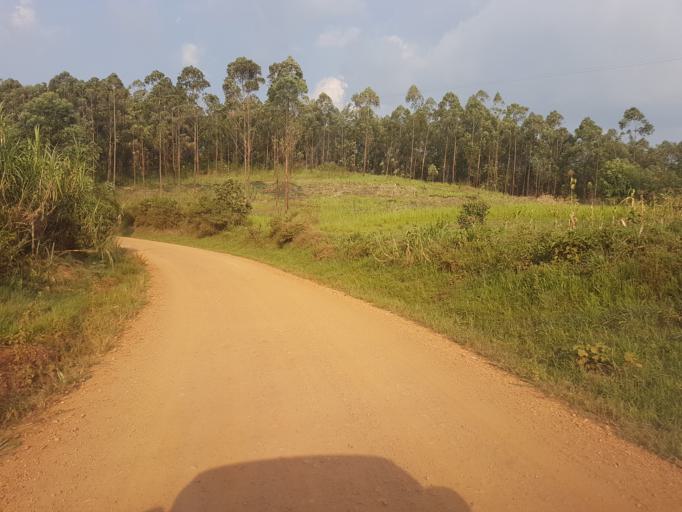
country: UG
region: Western Region
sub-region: Rukungiri District
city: Rukungiri
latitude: -0.6524
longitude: 29.8564
